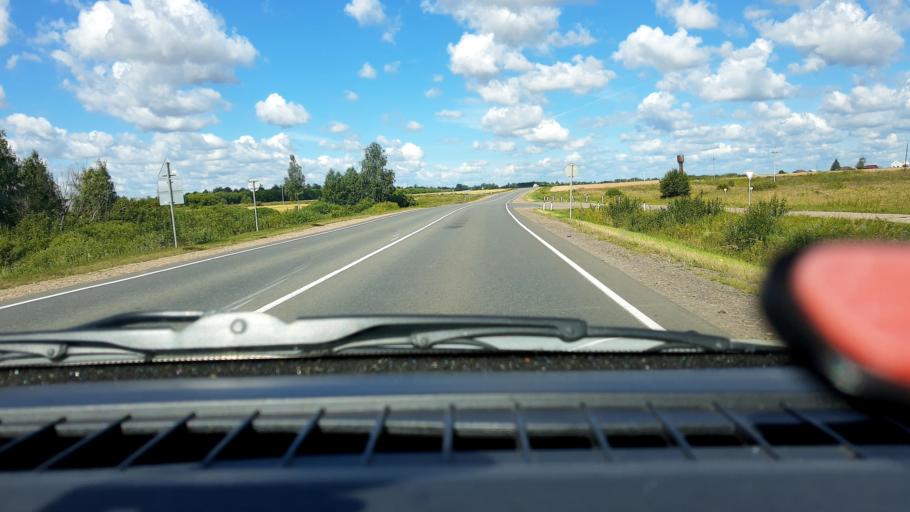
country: RU
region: Nizjnij Novgorod
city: Shatki
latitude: 55.2459
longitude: 44.0068
